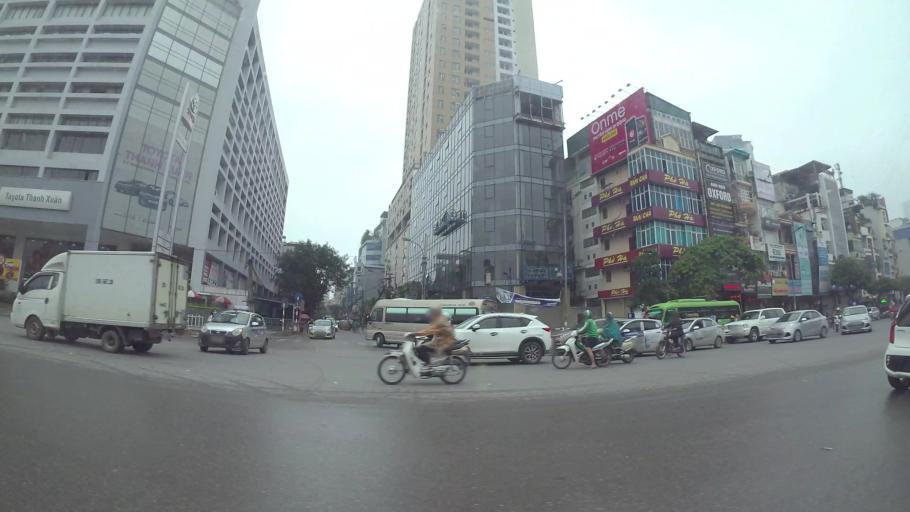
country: VN
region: Ha Noi
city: Dong Da
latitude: 21.0025
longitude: 105.8227
